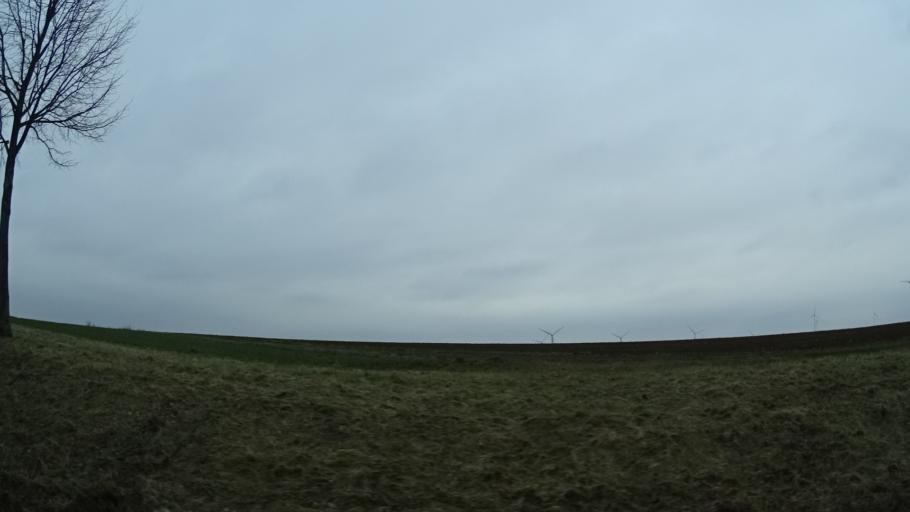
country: DE
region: Rheinland-Pfalz
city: Flomborn
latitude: 49.6898
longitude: 8.1455
